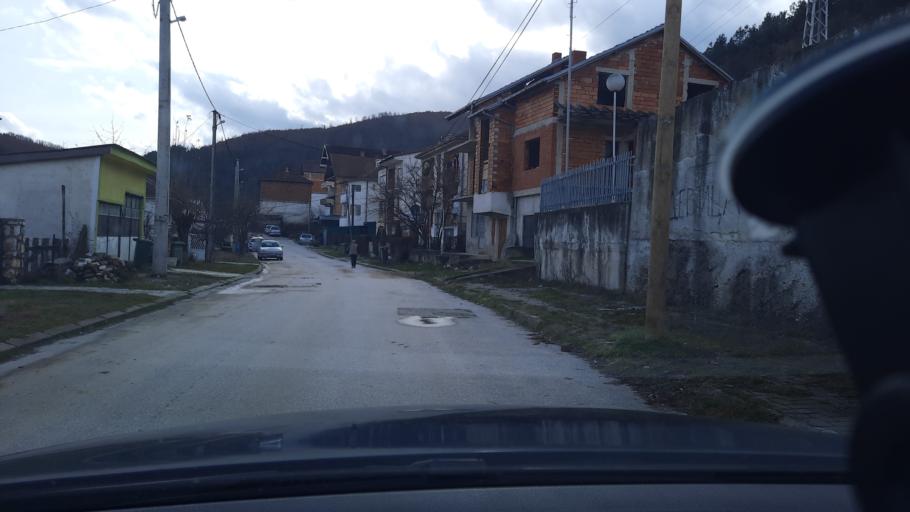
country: MK
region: Makedonski Brod
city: Makedonski Brod
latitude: 41.5104
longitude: 21.2151
